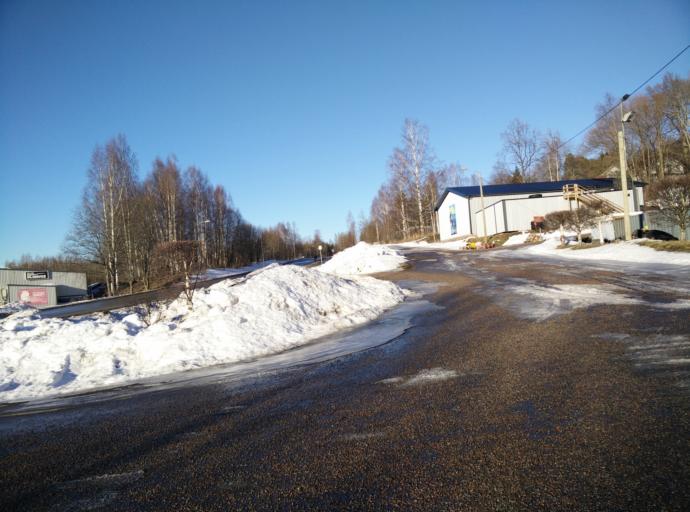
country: SE
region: Vaesternorrland
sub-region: Sundsvalls Kommun
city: Skottsund
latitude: 62.3124
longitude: 17.3930
